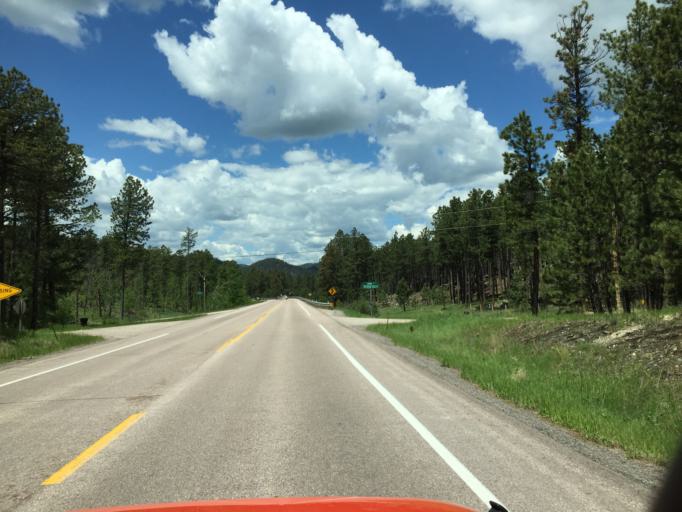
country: US
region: South Dakota
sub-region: Custer County
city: Custer
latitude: 43.8962
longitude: -103.5757
